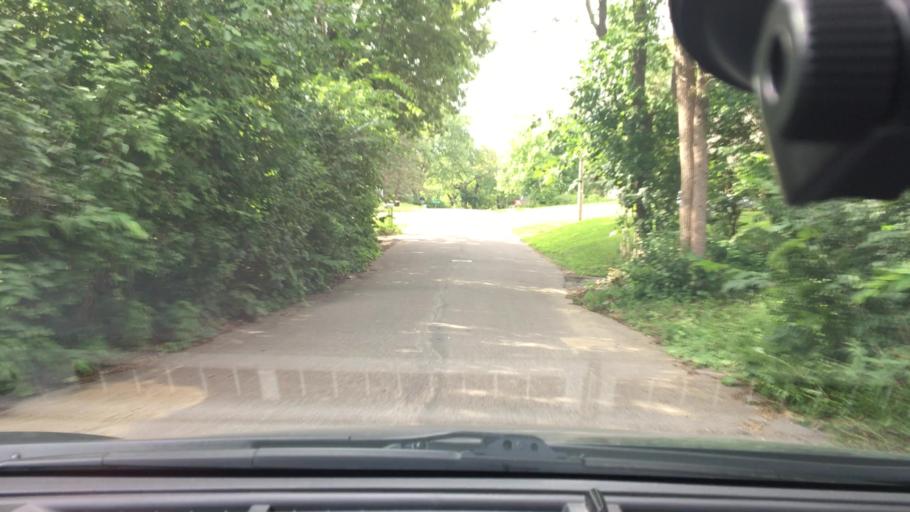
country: US
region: Minnesota
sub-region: Hennepin County
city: Plymouth
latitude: 45.0043
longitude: -93.4326
